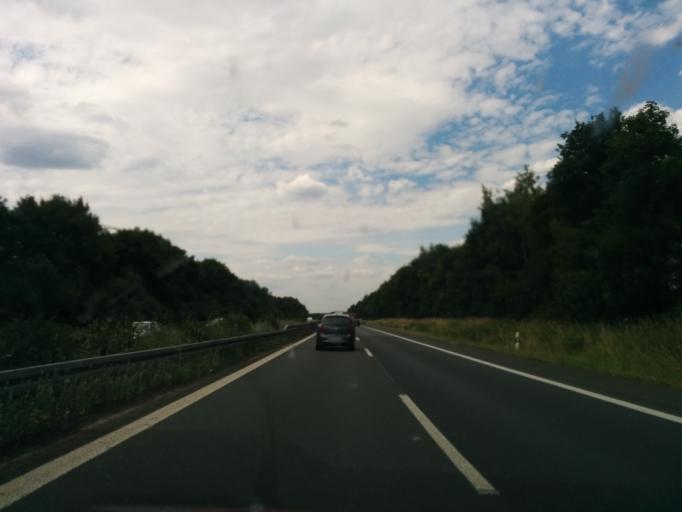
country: DE
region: Bavaria
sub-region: Upper Franconia
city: Eggolsheim
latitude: 49.7746
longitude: 11.0446
